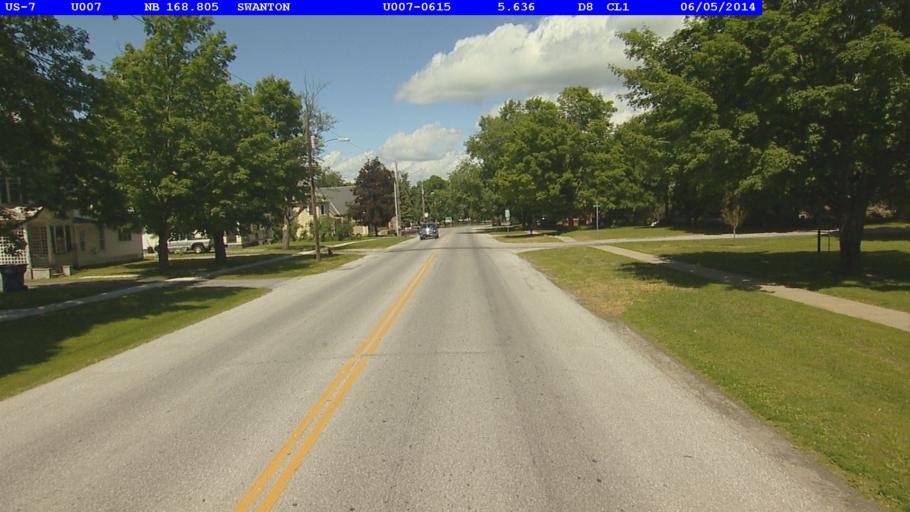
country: US
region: Vermont
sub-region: Franklin County
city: Swanton
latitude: 44.9169
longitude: -73.1222
